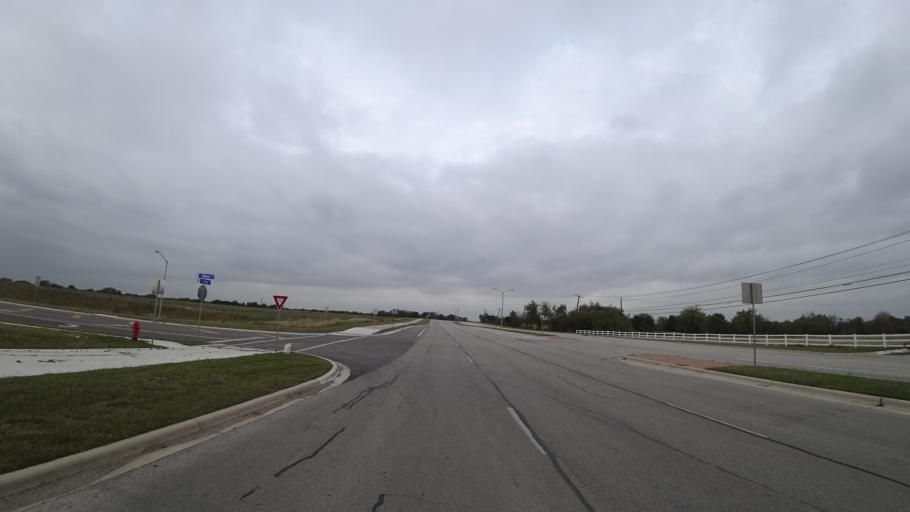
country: US
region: Texas
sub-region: Travis County
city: Pflugerville
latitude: 30.4256
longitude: -97.5929
